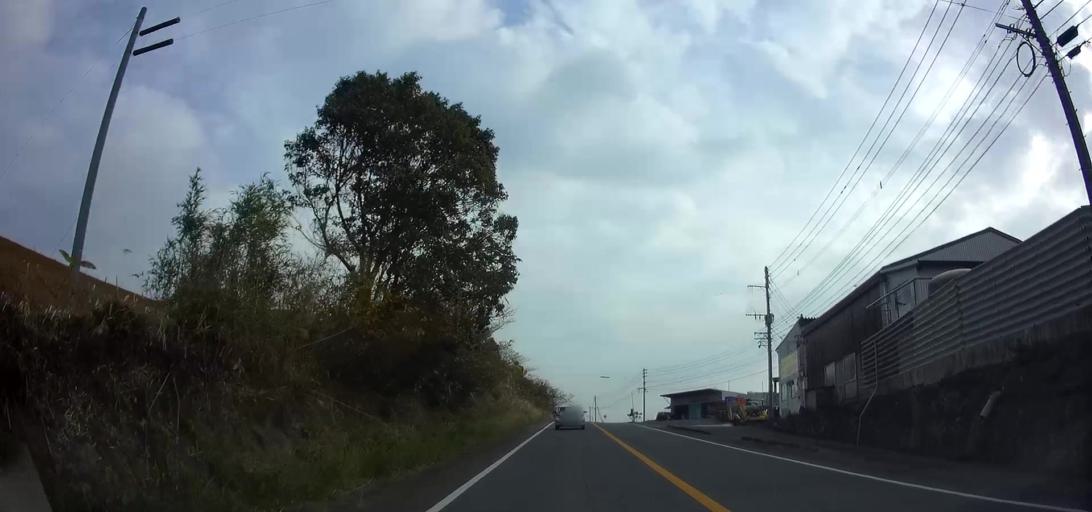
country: JP
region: Nagasaki
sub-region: Isahaya-shi
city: Isahaya
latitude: 32.7909
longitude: 130.0573
